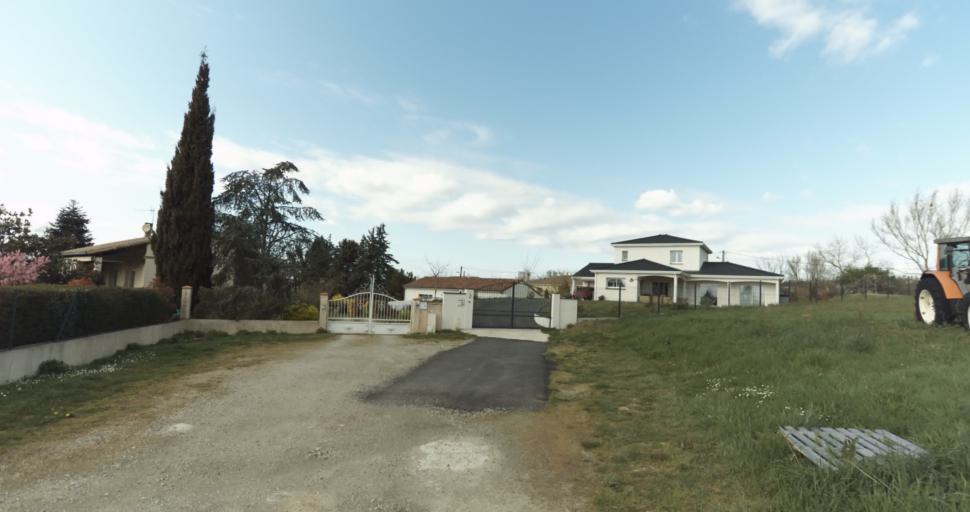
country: FR
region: Midi-Pyrenees
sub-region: Departement de la Haute-Garonne
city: Auterive
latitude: 43.3490
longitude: 1.4865
